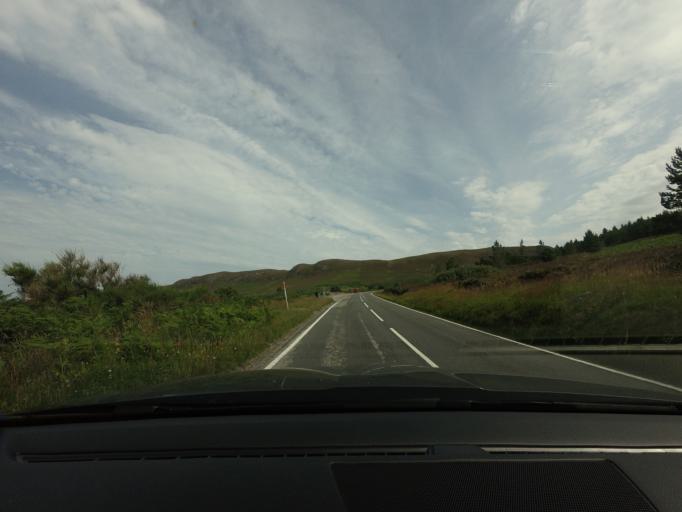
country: GB
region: Scotland
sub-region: Highland
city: Alness
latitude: 57.8414
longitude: -4.2729
